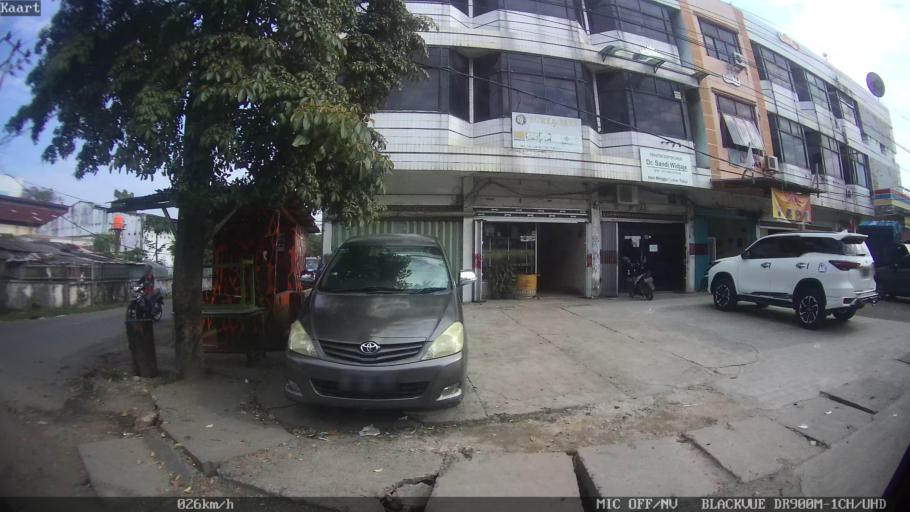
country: ID
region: Lampung
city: Bandarlampung
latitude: -5.4459
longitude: 105.2754
